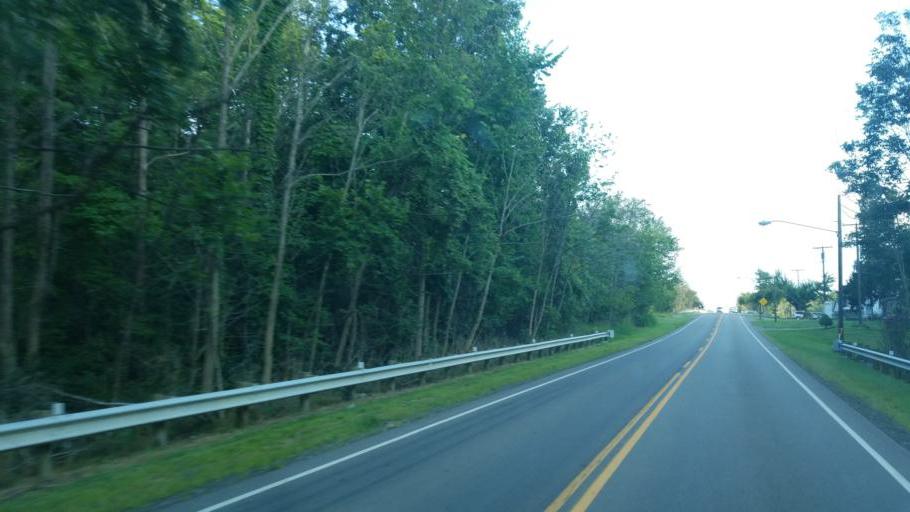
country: US
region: Ohio
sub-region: Huron County
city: Willard
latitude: 41.0606
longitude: -82.7165
